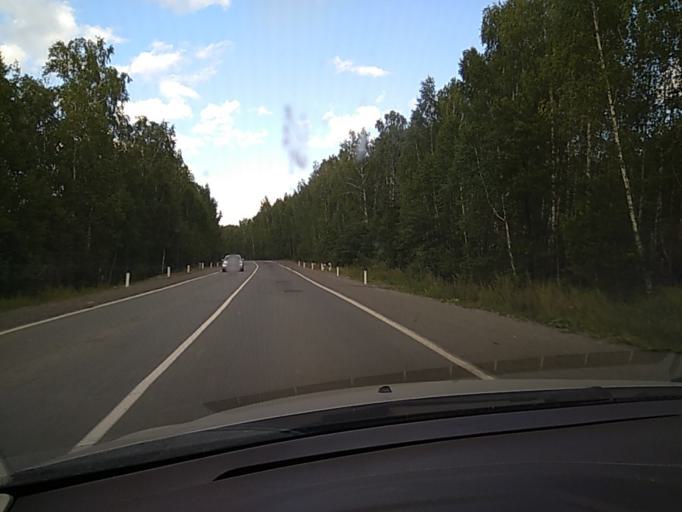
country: RU
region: Chelyabinsk
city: Karabash
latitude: 55.4976
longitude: 60.2526
